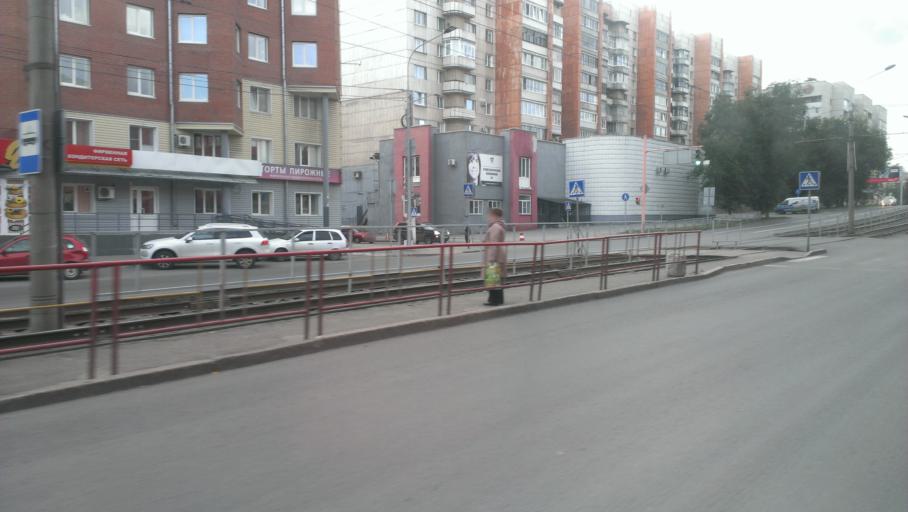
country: RU
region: Altai Krai
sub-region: Gorod Barnaulskiy
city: Barnaul
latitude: 53.3427
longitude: 83.7690
